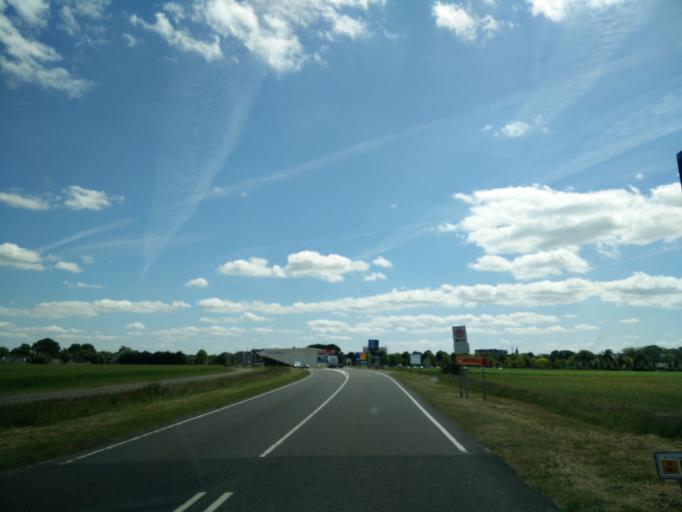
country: NL
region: Drenthe
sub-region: Gemeente Emmen
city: Emmen
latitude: 52.7883
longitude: 6.8829
